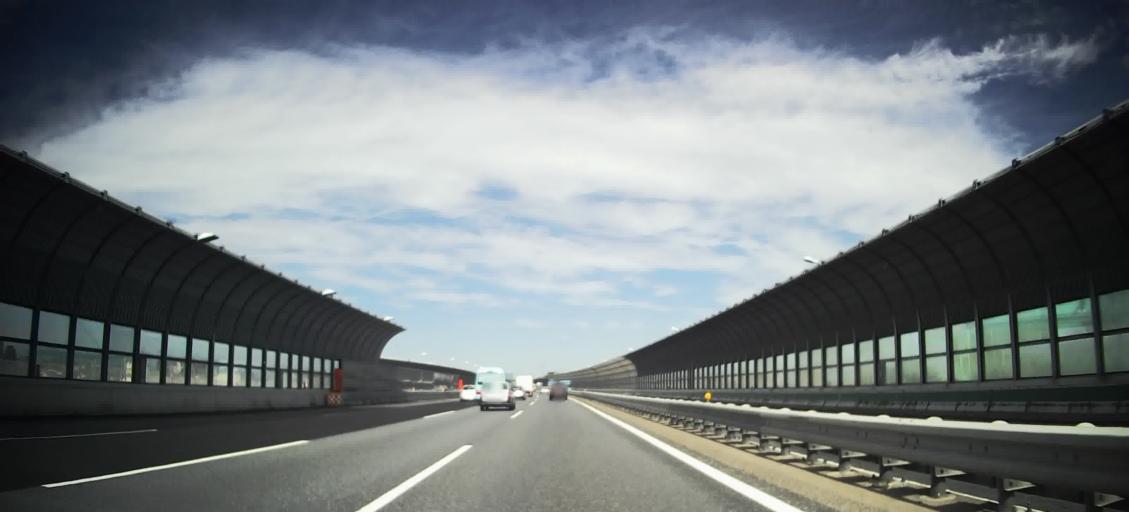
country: JP
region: Saitama
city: Wako
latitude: 35.7571
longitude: 139.6012
